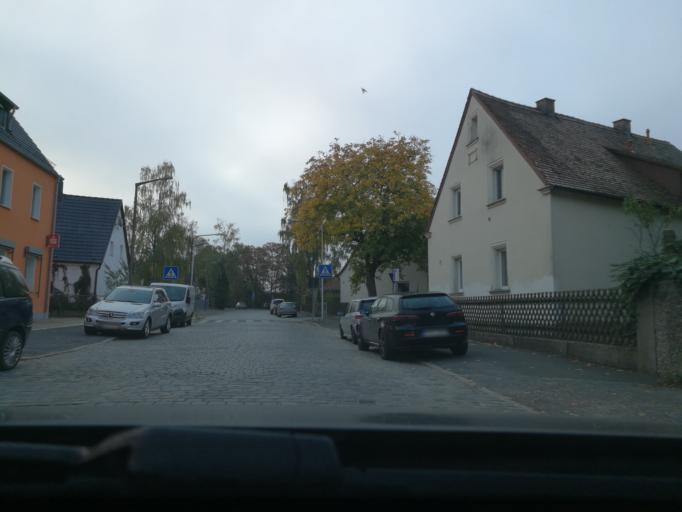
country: DE
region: Bavaria
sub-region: Regierungsbezirk Mittelfranken
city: Wetzendorf
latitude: 49.4957
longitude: 11.0477
